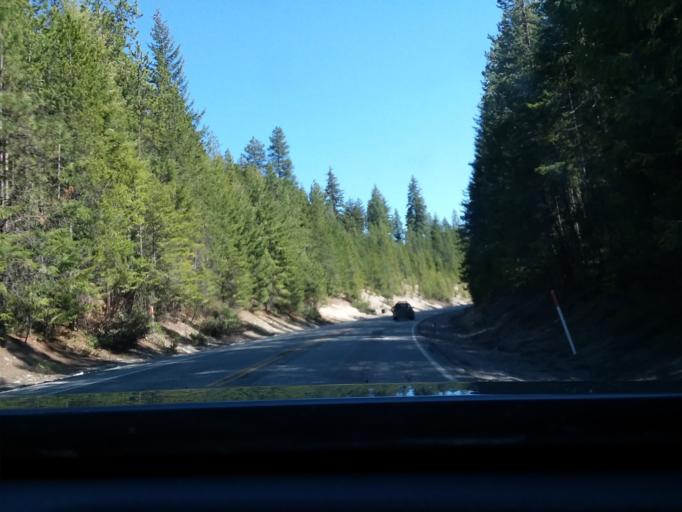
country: US
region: Washington
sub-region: Chelan County
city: Leavenworth
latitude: 47.7948
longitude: -120.6627
